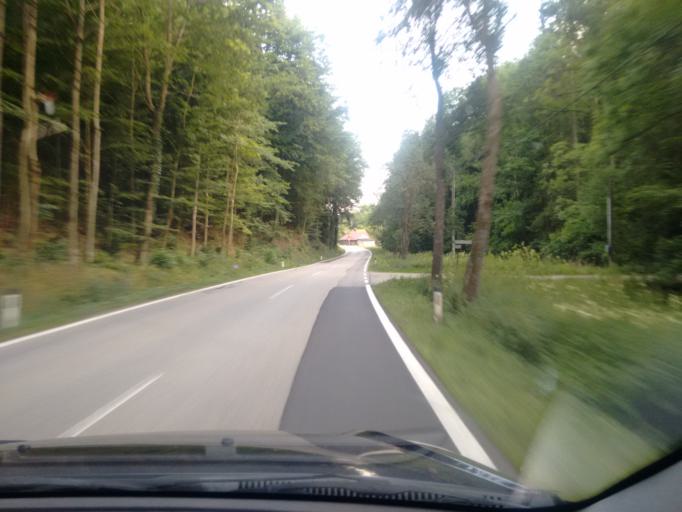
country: AT
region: Upper Austria
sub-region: Politischer Bezirk Urfahr-Umgebung
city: Feldkirchen an der Donau
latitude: 48.3778
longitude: 14.0634
